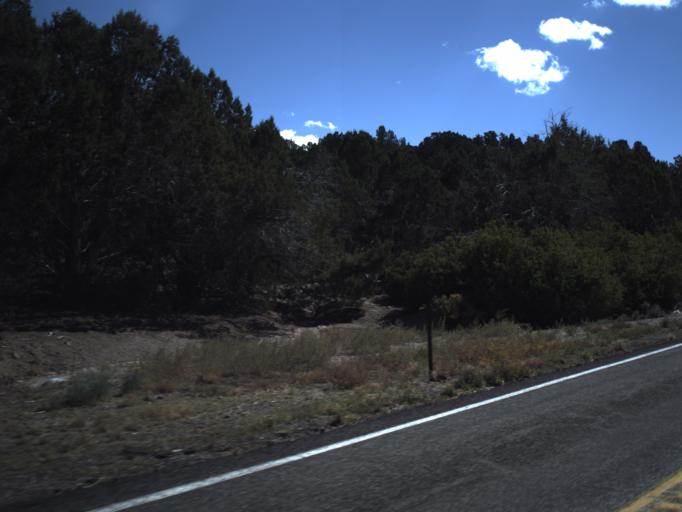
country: US
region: Utah
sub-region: Washington County
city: Enterprise
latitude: 37.5429
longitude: -113.6829
